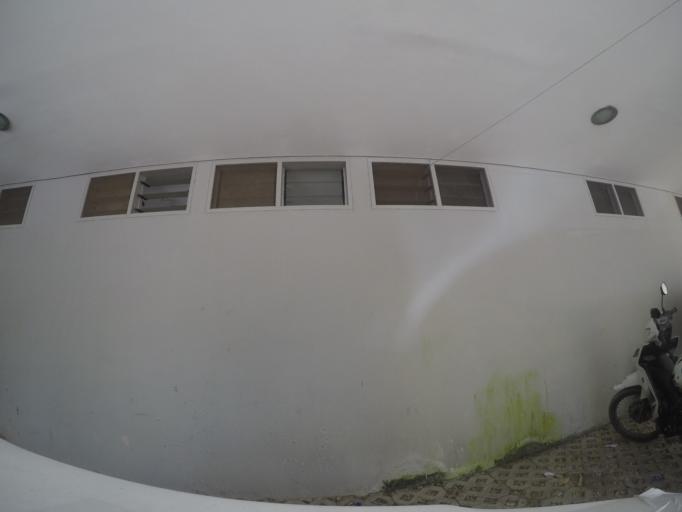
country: TL
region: Baucau
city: Baucau
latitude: -8.4612
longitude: 126.4500
